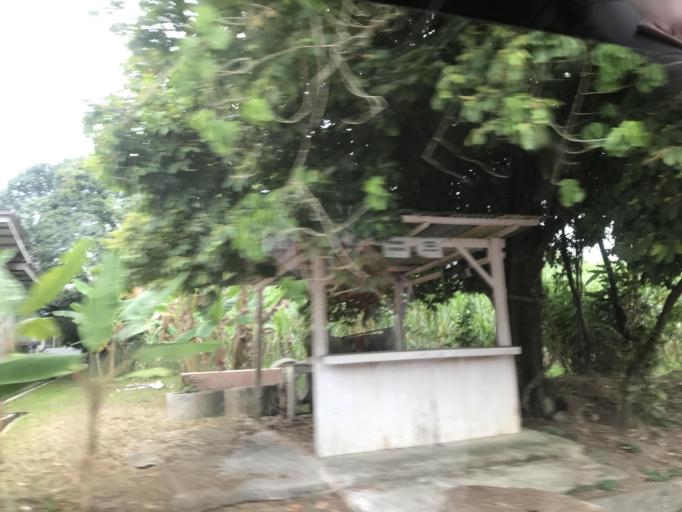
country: MY
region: Kelantan
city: Kota Bharu
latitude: 6.1192
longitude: 102.2059
